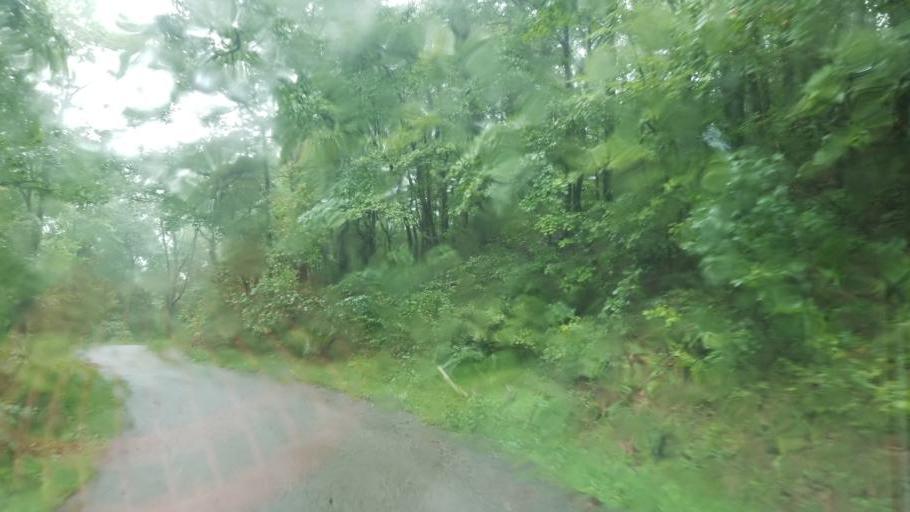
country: US
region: Ohio
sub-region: Scioto County
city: West Portsmouth
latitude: 38.7777
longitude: -83.1656
